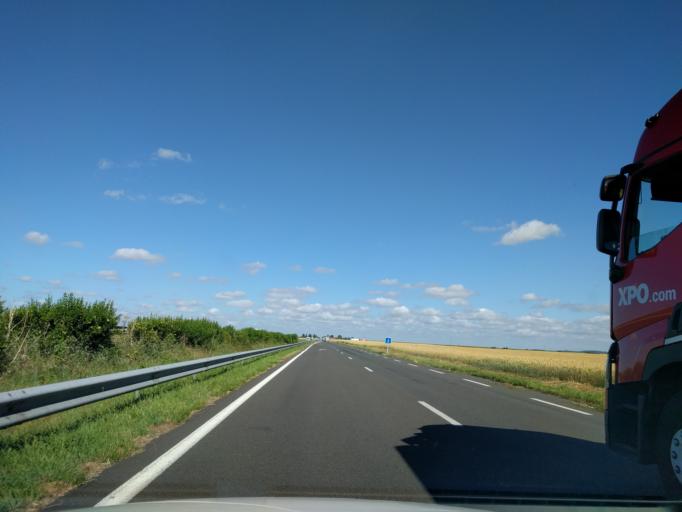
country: FR
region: Pays de la Loire
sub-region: Departement de la Vendee
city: Maillezais
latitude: 46.4265
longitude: -0.7205
